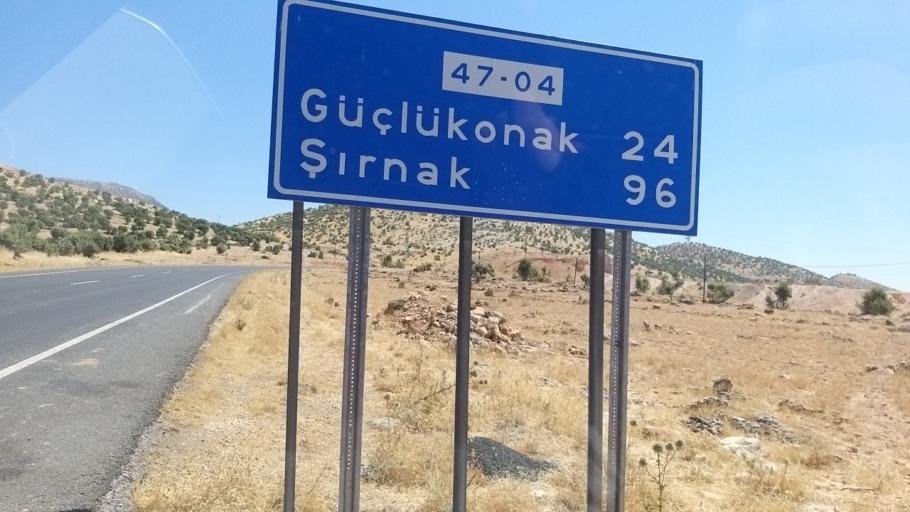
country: TR
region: Mardin
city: Dargecit
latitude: 37.5490
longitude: 41.7485
